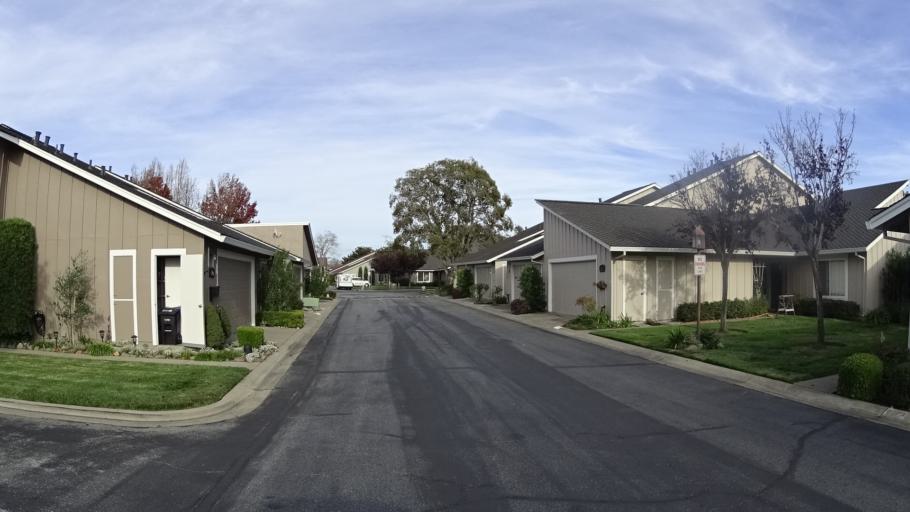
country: US
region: California
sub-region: San Mateo County
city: Foster City
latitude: 37.5440
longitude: -122.2643
